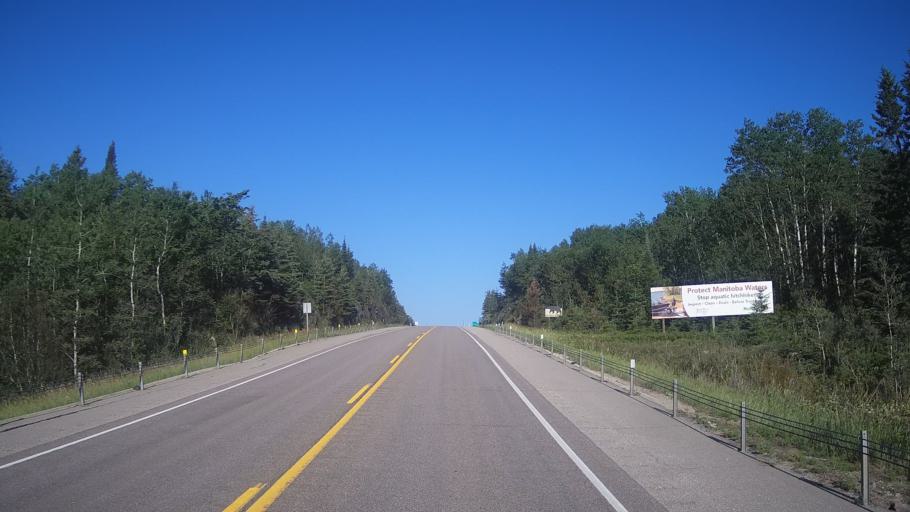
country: US
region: Minnesota
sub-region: Roseau County
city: Warroad
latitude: 49.7372
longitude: -95.2002
